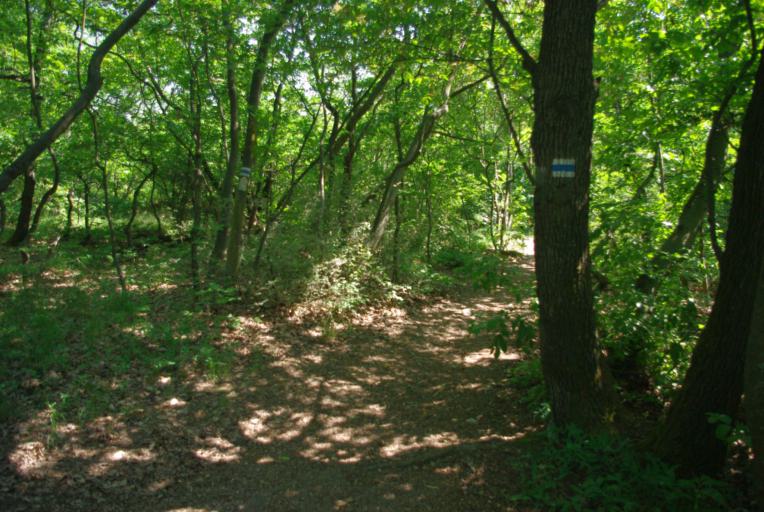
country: HU
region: Pest
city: Pilisborosjeno
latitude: 47.5987
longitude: 18.9868
